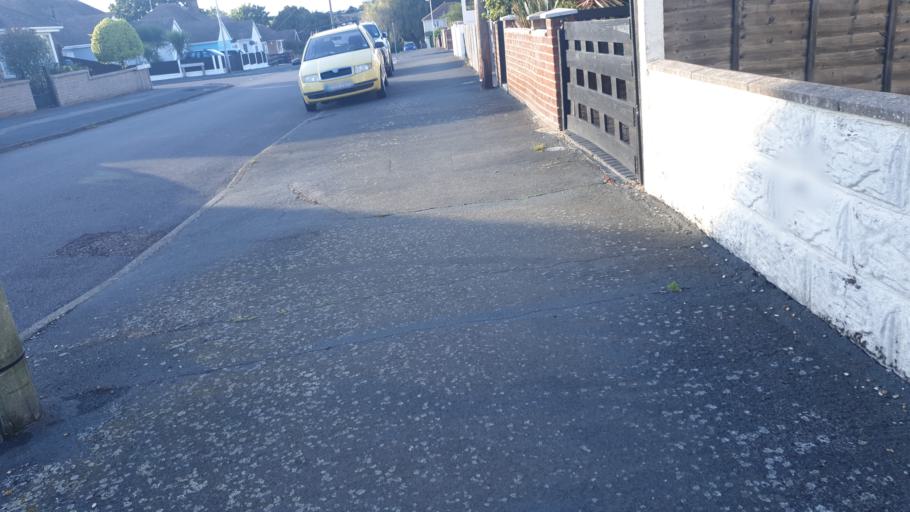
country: GB
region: England
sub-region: Essex
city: Clacton-on-Sea
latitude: 51.8045
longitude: 1.1803
